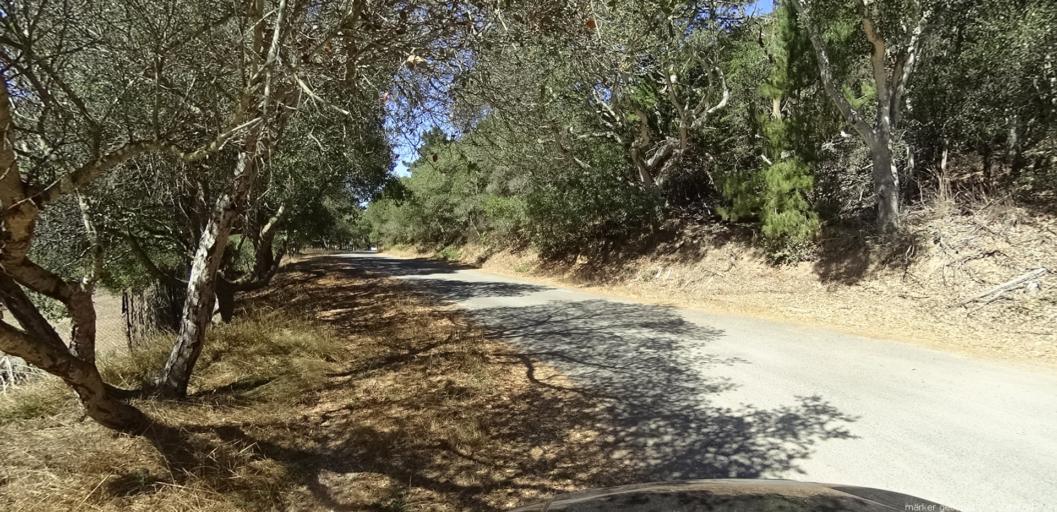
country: US
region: California
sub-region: Monterey County
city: Elkhorn
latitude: 36.8300
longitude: -121.6932
